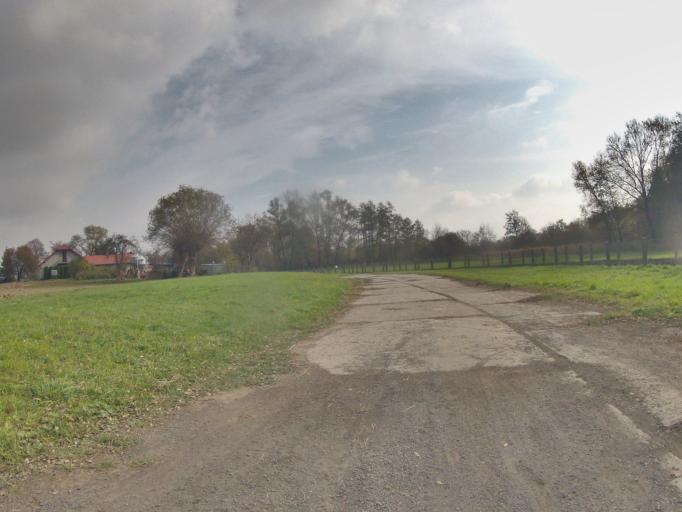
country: PL
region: Lesser Poland Voivodeship
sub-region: Powiat wielicki
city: Wegrzce Wielkie
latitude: 50.0533
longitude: 20.1109
